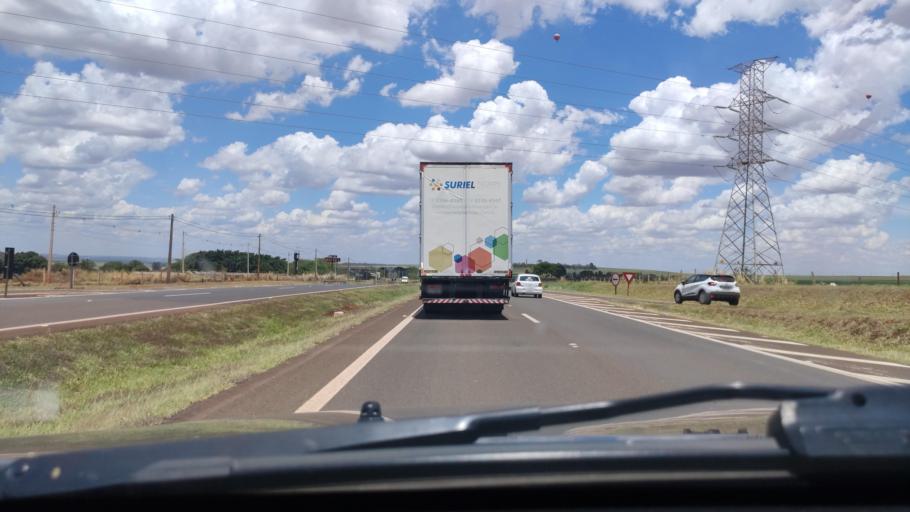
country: BR
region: Sao Paulo
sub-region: Jau
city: Jau
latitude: -22.3038
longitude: -48.5957
